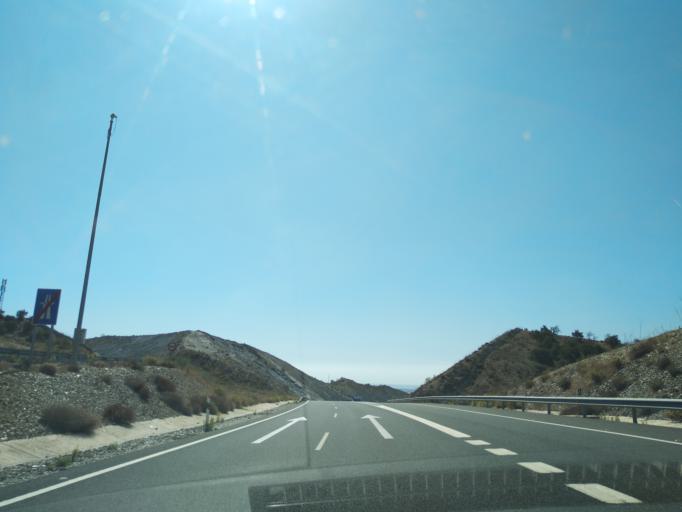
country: ES
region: Andalusia
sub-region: Provincia de Malaga
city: Malaga
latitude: 36.7605
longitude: -4.4885
